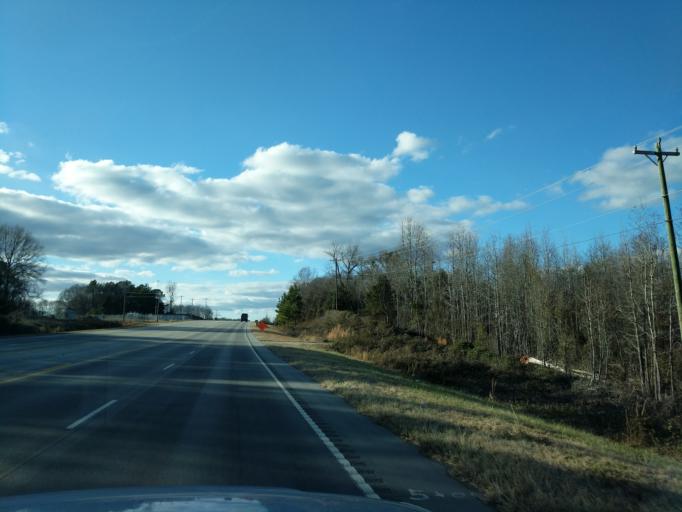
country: US
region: South Carolina
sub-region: Spartanburg County
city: Woodruff
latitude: 34.7815
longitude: -82.0968
